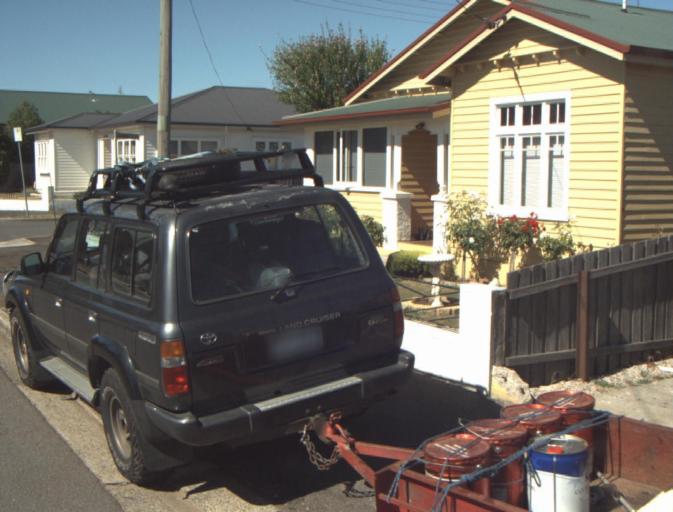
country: AU
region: Tasmania
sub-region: Launceston
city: Newnham
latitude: -41.4139
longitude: 147.1323
